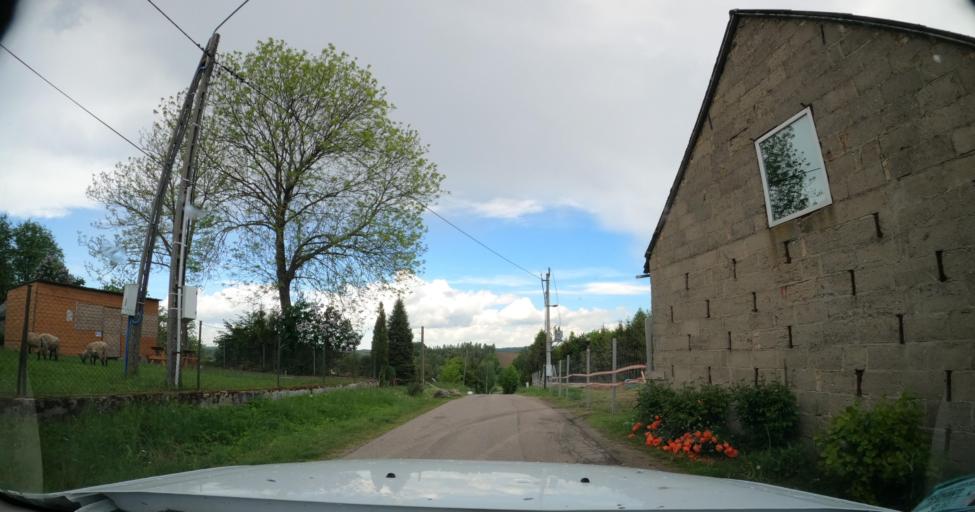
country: PL
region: Pomeranian Voivodeship
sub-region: Powiat kartuski
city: Garcz
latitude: 54.3331
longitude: 18.1395
